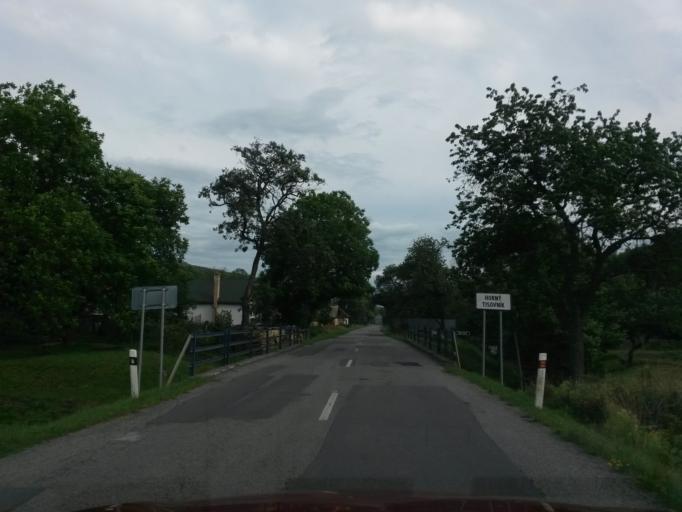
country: SK
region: Banskobystricky
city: Detva
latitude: 48.4197
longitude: 19.3593
